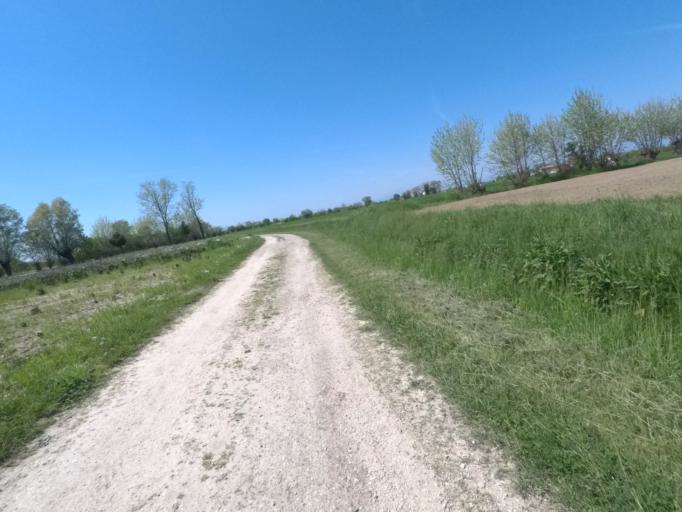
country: IT
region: Veneto
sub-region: Provincia di Treviso
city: Piavon
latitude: 45.7854
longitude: 12.5275
